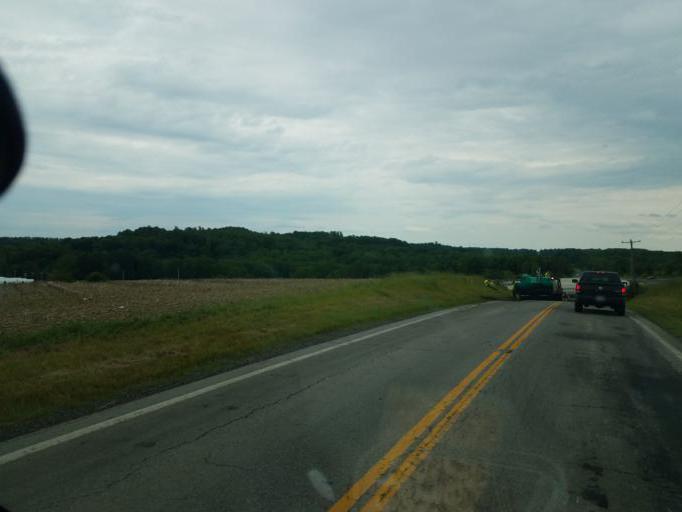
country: US
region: Ohio
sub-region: Richland County
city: Lexington
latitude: 40.6042
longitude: -82.5861
